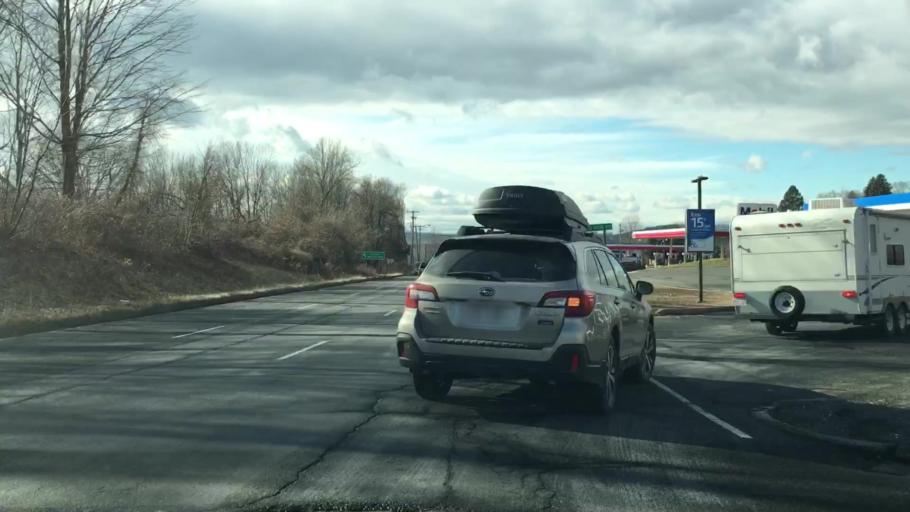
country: US
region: Connecticut
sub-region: Fairfield County
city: Bethel
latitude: 41.4199
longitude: -73.4052
